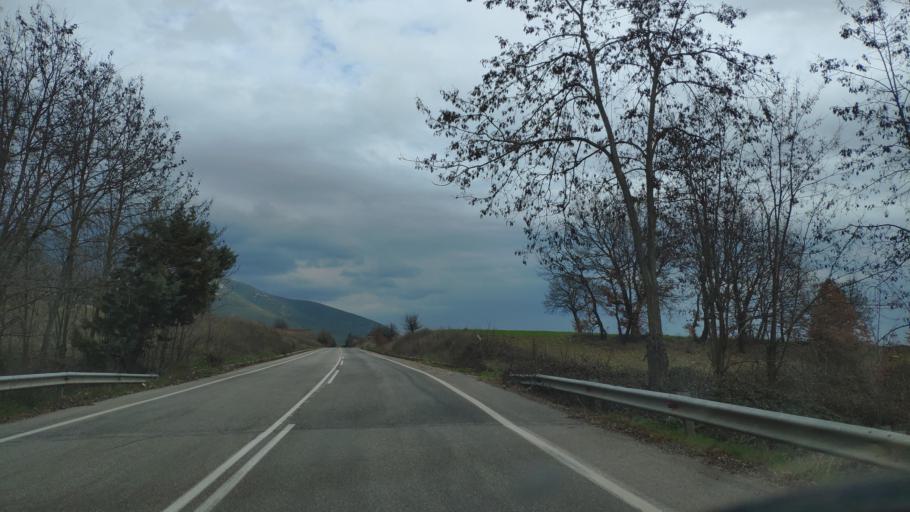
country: GR
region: Central Greece
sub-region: Nomos Fthiotidos
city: Anthili
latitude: 38.7108
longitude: 22.4675
